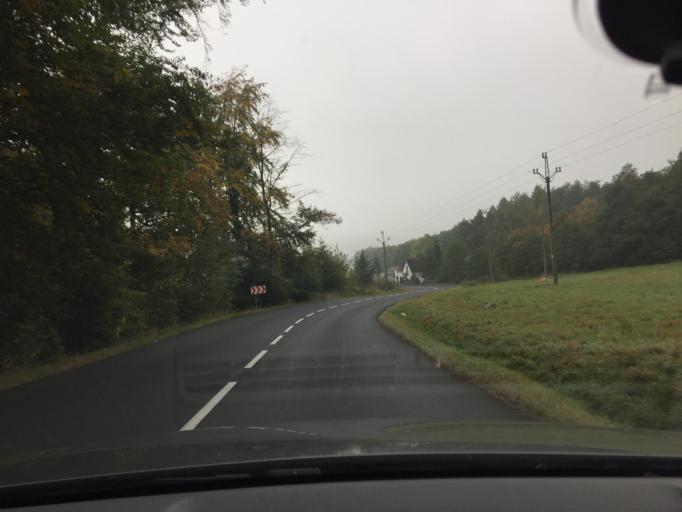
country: CZ
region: Ustecky
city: Libouchec
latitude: 50.7722
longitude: 14.0402
